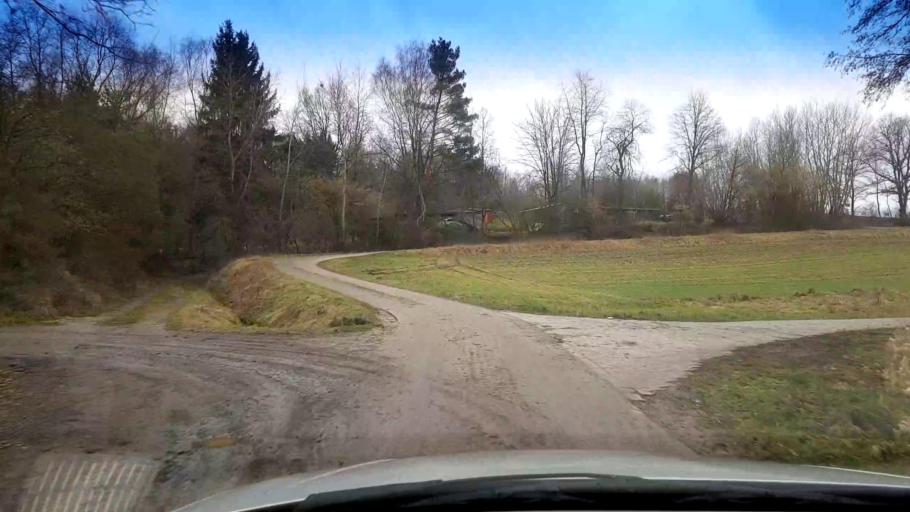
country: DE
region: Bavaria
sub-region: Upper Franconia
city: Baunach
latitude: 49.9804
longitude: 10.8359
